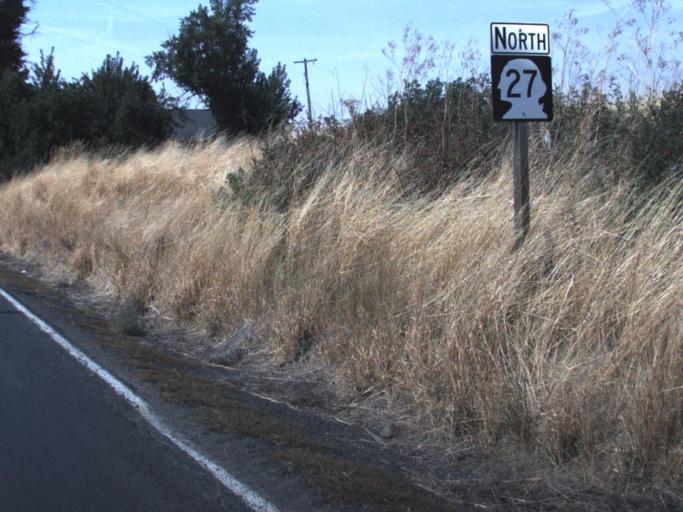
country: US
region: Idaho
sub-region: Benewah County
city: Plummer
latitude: 47.2296
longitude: -117.0859
